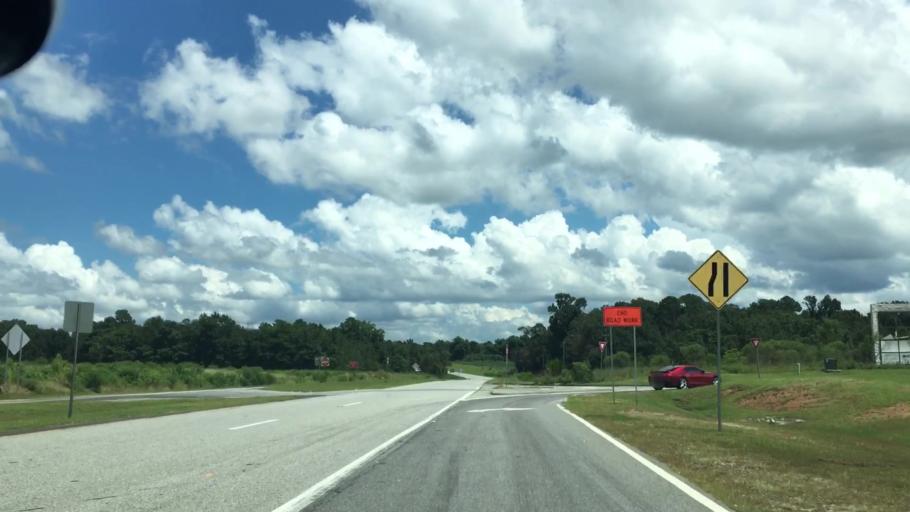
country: US
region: Georgia
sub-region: Crisp County
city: Cordele
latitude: 31.9358
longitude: -83.7453
